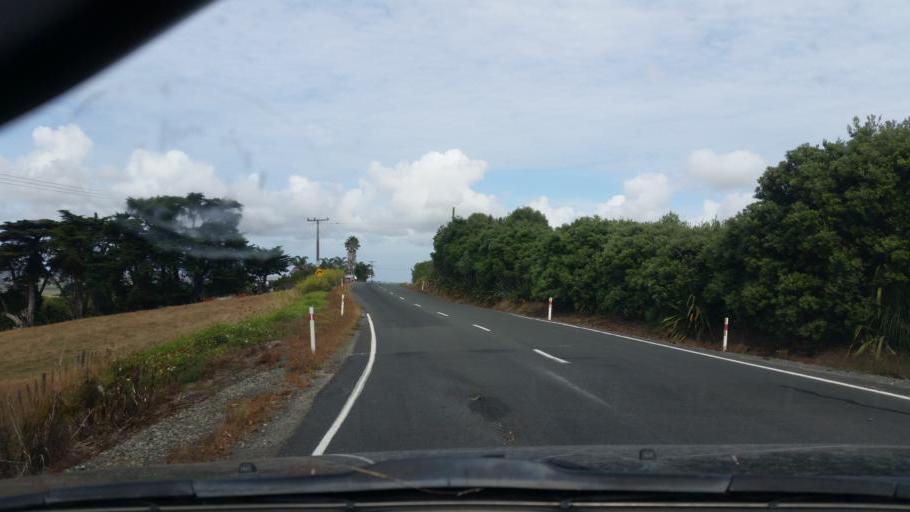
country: NZ
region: Northland
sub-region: Kaipara District
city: Dargaville
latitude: -35.9486
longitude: 173.9100
